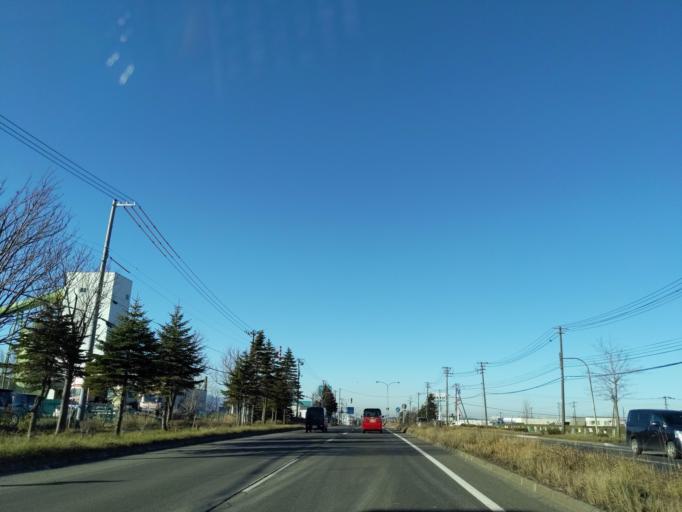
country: JP
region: Hokkaido
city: Kitahiroshima
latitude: 42.9615
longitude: 141.4912
